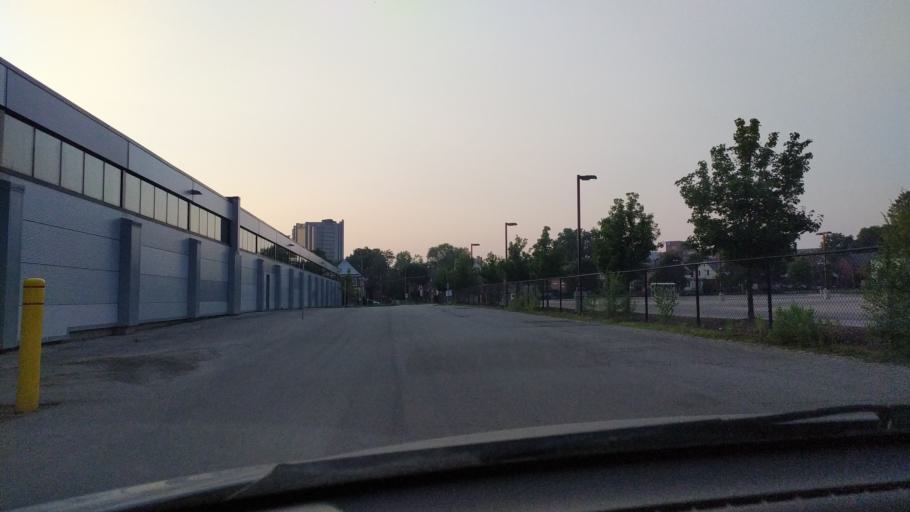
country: CA
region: Ontario
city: Waterloo
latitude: 43.4520
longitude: -80.5126
